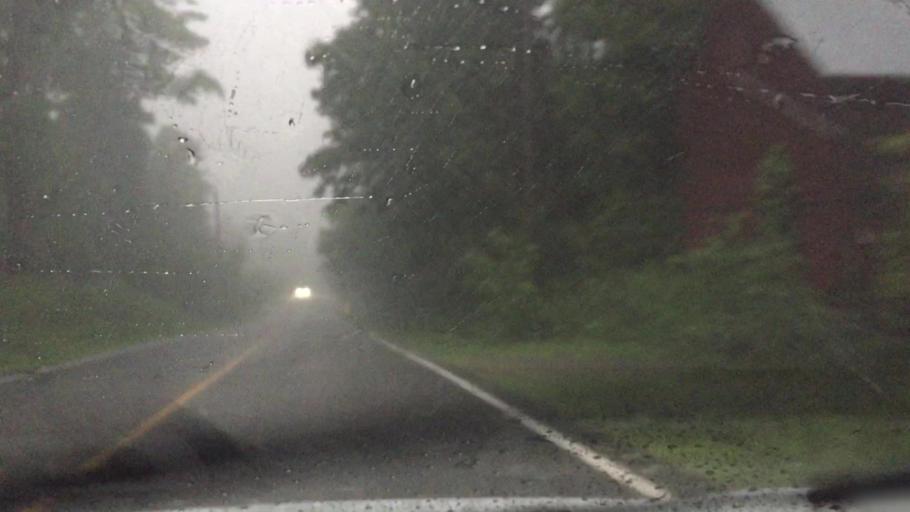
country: CA
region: Ontario
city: Markham
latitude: 43.8582
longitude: -79.2041
